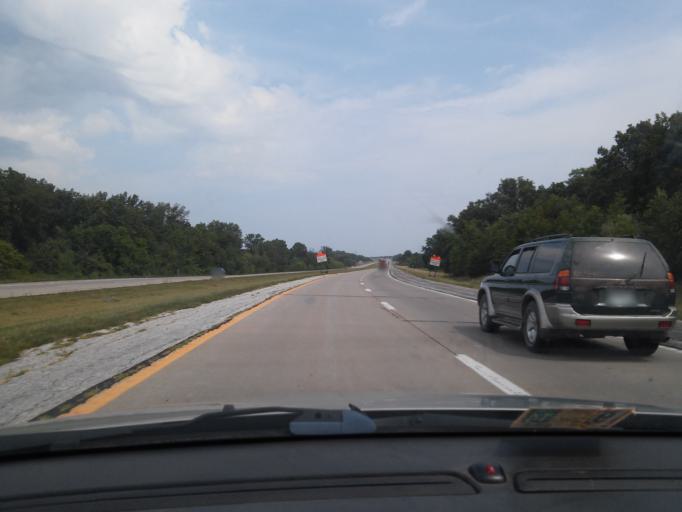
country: US
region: Missouri
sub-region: Audrain County
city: Mexico
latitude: 39.0419
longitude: -91.8932
